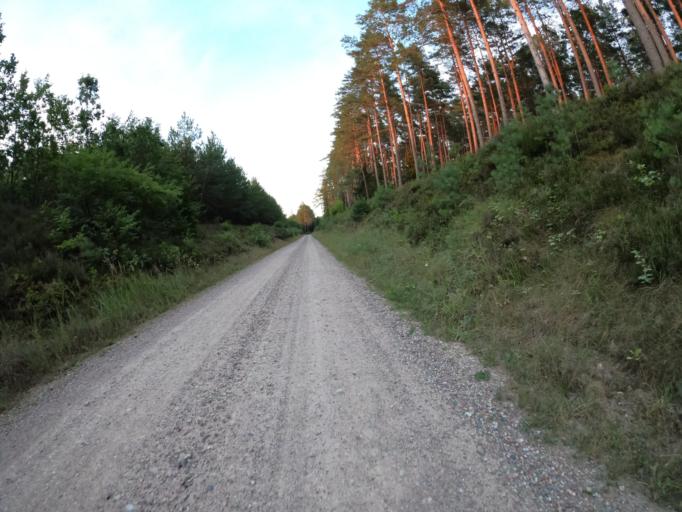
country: PL
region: West Pomeranian Voivodeship
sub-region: Powiat koszalinski
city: Sianow
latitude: 54.1008
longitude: 16.4019
